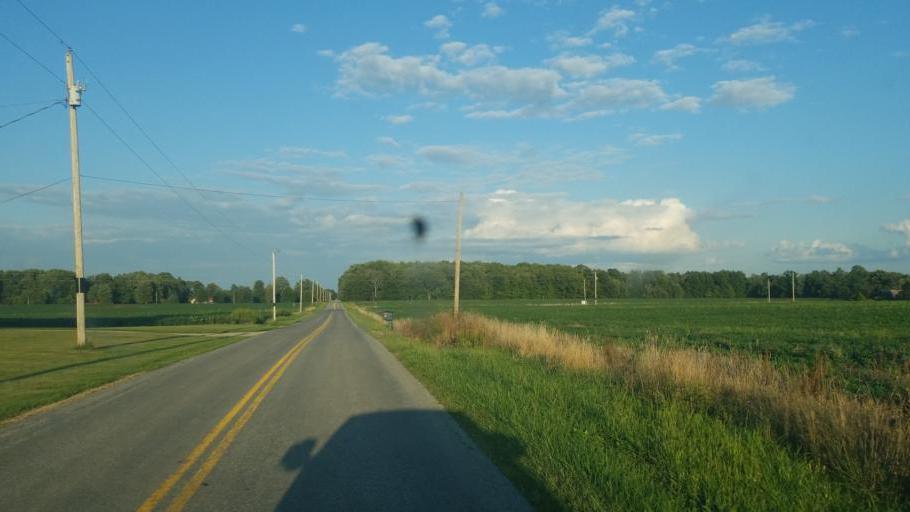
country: US
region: Ohio
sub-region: Huron County
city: Greenwich
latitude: 41.0523
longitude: -82.5633
